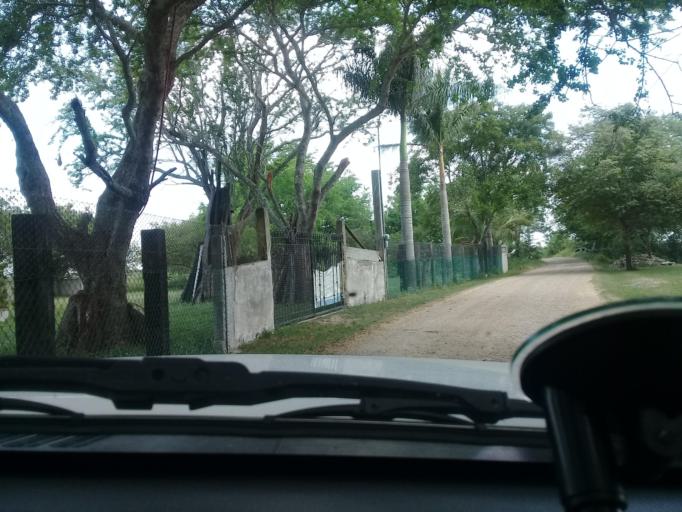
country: MX
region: Veracruz
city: Moralillo
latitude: 22.1767
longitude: -98.0167
